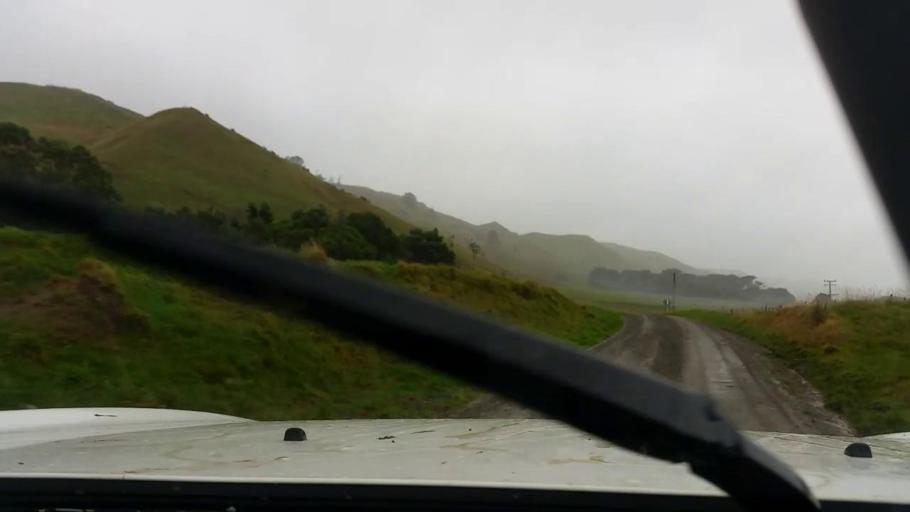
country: NZ
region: Wellington
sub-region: Masterton District
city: Masterton
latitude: -41.2611
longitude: 175.8962
